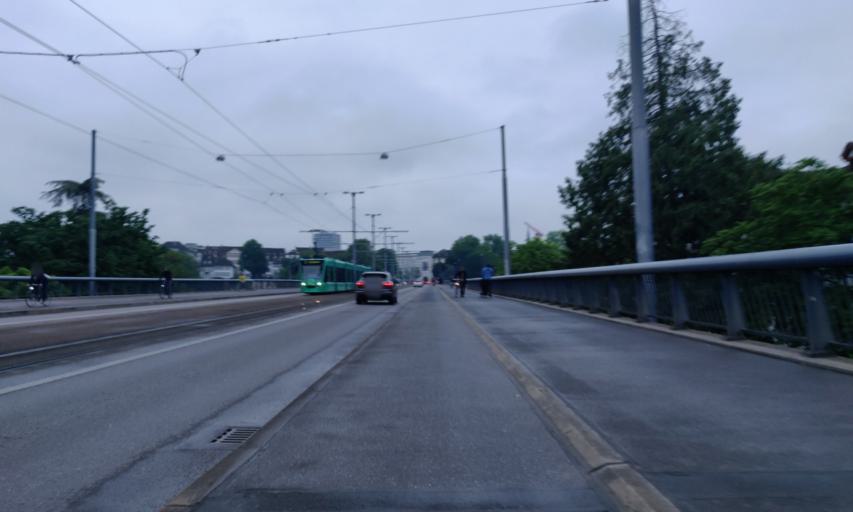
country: CH
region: Basel-City
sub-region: Basel-Stadt
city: Basel
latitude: 47.5580
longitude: 7.5972
